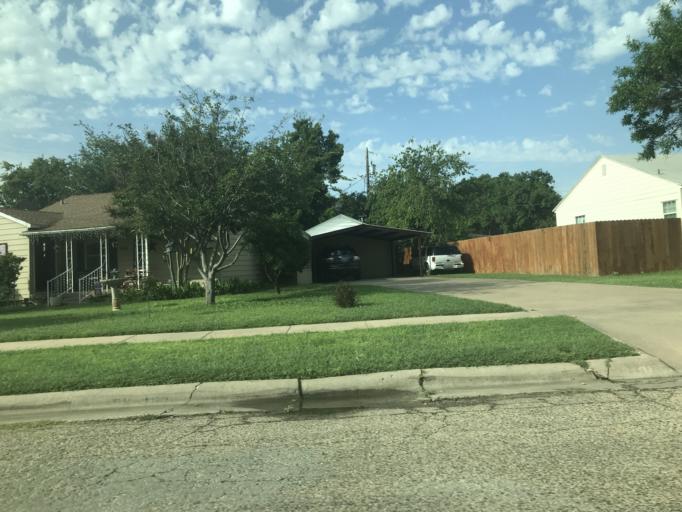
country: US
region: Texas
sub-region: Taylor County
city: Abilene
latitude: 32.4285
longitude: -99.7596
